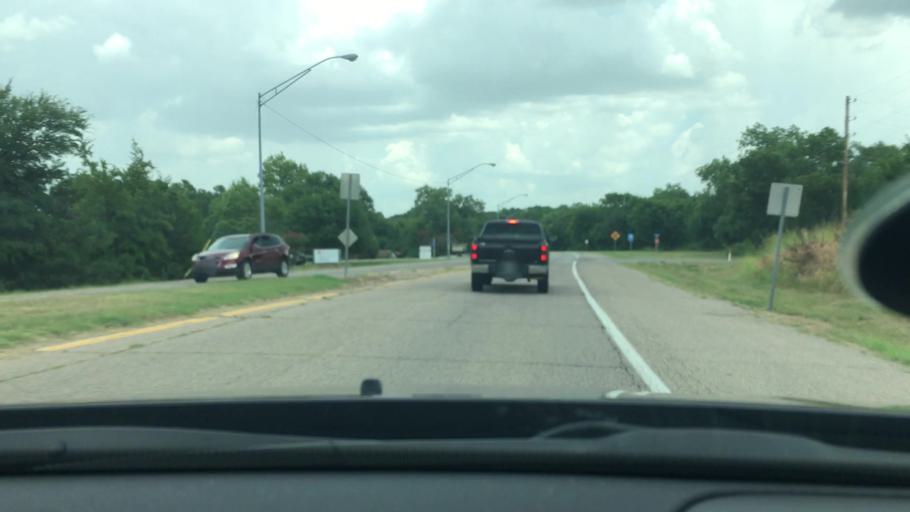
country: US
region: Oklahoma
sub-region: Marshall County
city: Madill
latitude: 34.0785
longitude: -96.7795
